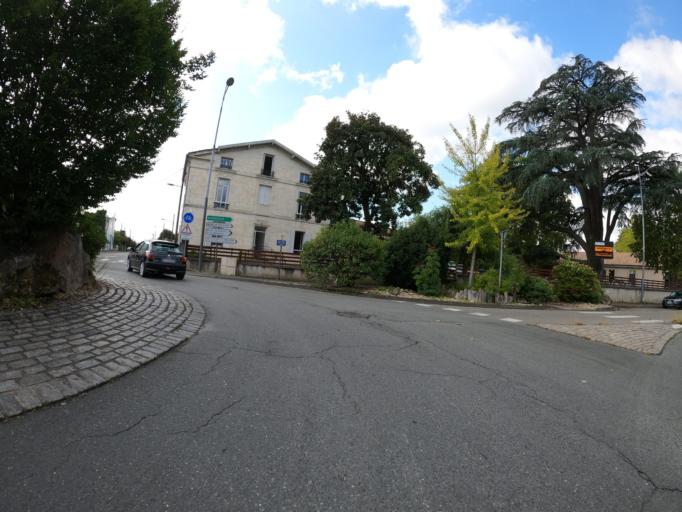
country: FR
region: Aquitaine
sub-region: Departement de la Dordogne
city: Bergerac
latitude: 44.8450
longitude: 0.4809
